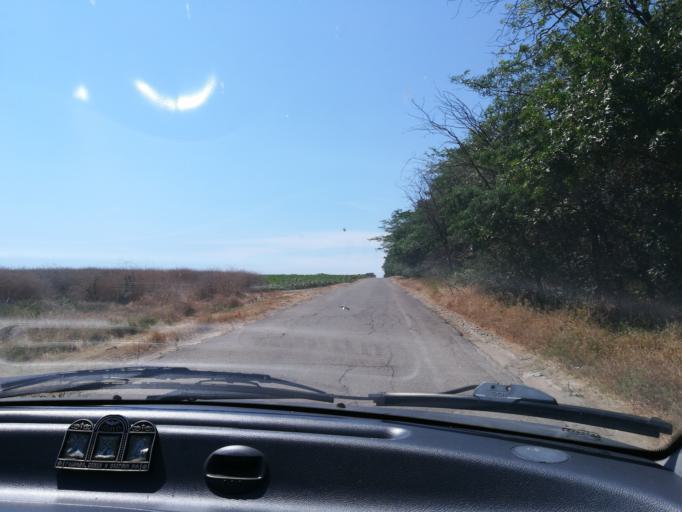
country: RU
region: Krasnodarskiy
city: Blagovetschenskaya
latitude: 45.0564
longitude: 37.1106
